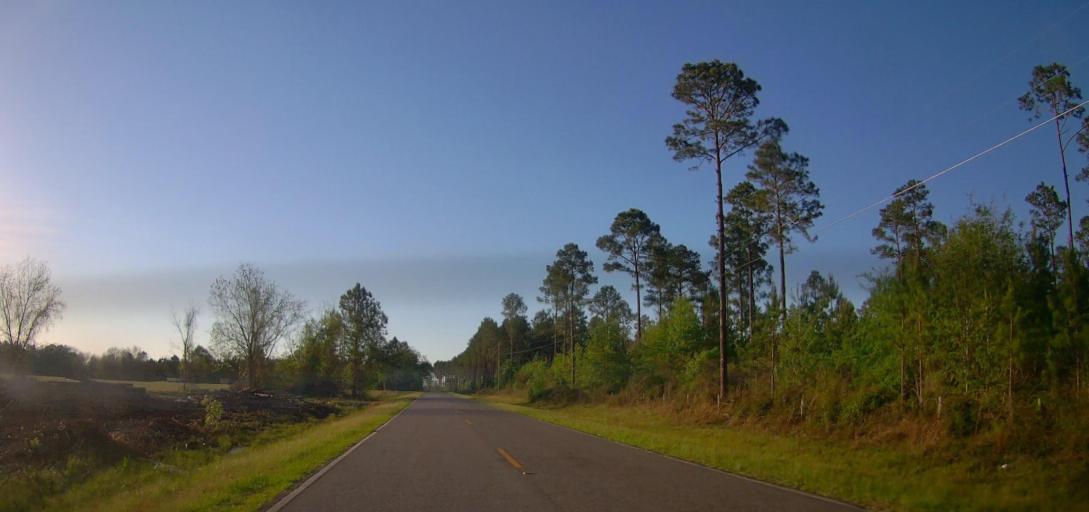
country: US
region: Georgia
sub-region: Ben Hill County
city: Fitzgerald
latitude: 31.6746
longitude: -83.2153
